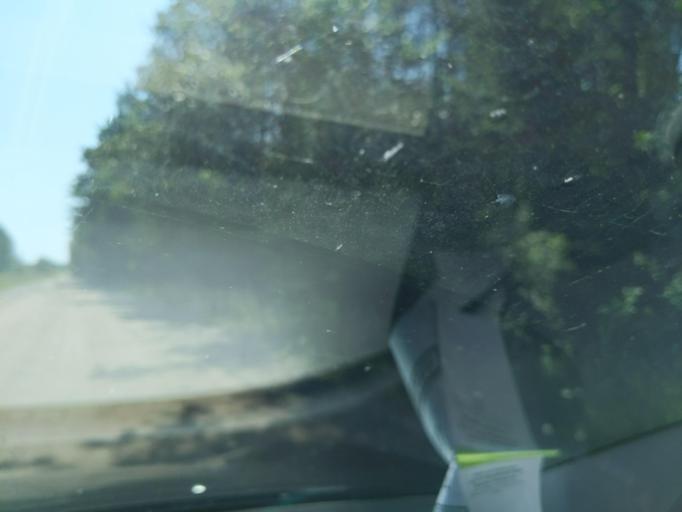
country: US
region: Michigan
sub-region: Mackinac County
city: Saint Ignace
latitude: 45.6796
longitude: -84.7113
